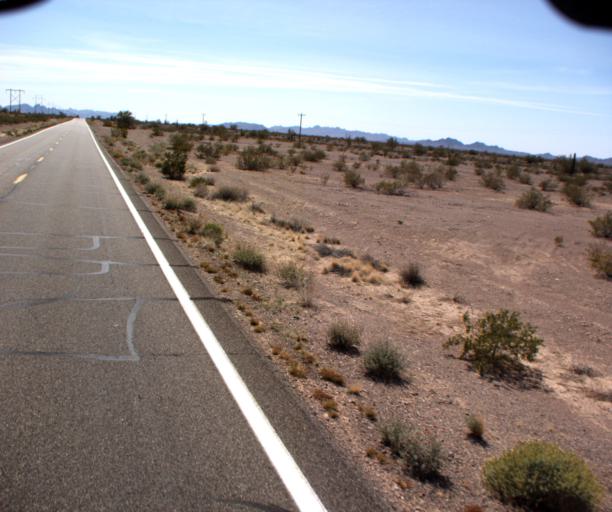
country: US
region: Arizona
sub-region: La Paz County
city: Quartzsite
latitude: 33.4682
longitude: -114.2170
